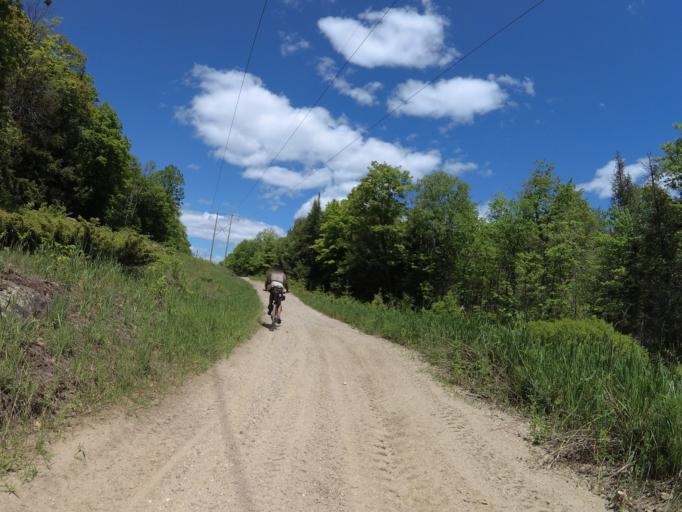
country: CA
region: Ontario
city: Renfrew
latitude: 45.0225
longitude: -76.8886
